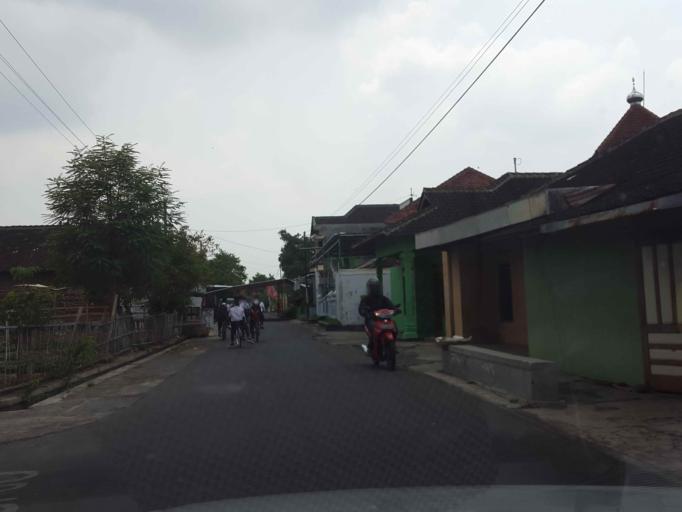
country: ID
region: Central Java
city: Jaten
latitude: -7.5998
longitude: 110.9435
